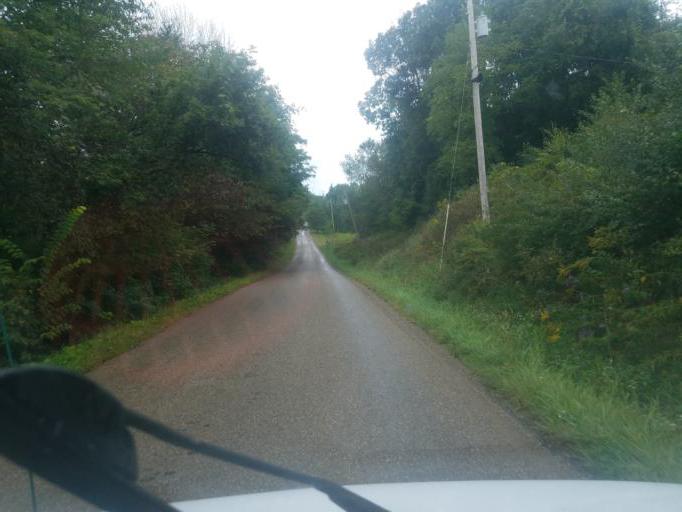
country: US
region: Ohio
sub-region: Wayne County
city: West Salem
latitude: 40.9503
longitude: -82.1054
